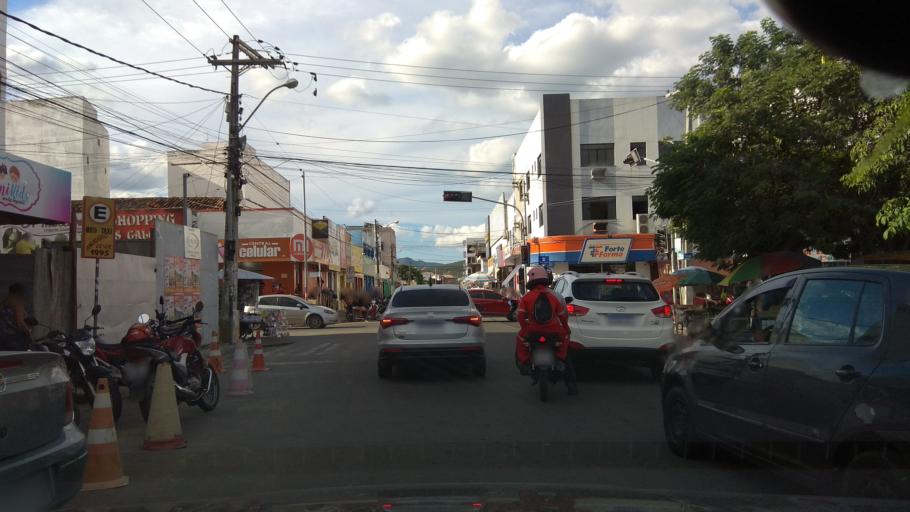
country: BR
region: Bahia
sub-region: Jequie
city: Jequie
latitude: -13.8611
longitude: -40.0788
